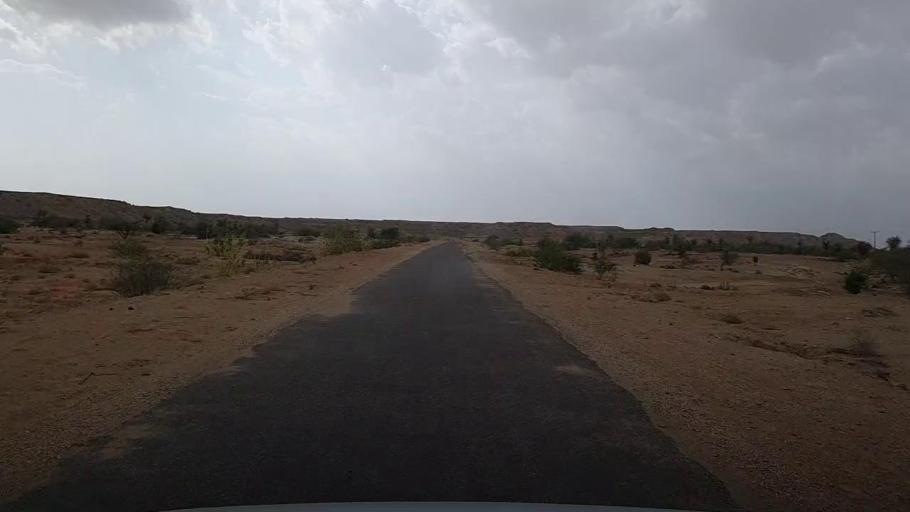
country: PK
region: Sindh
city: Jamshoro
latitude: 25.4159
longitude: 67.6970
